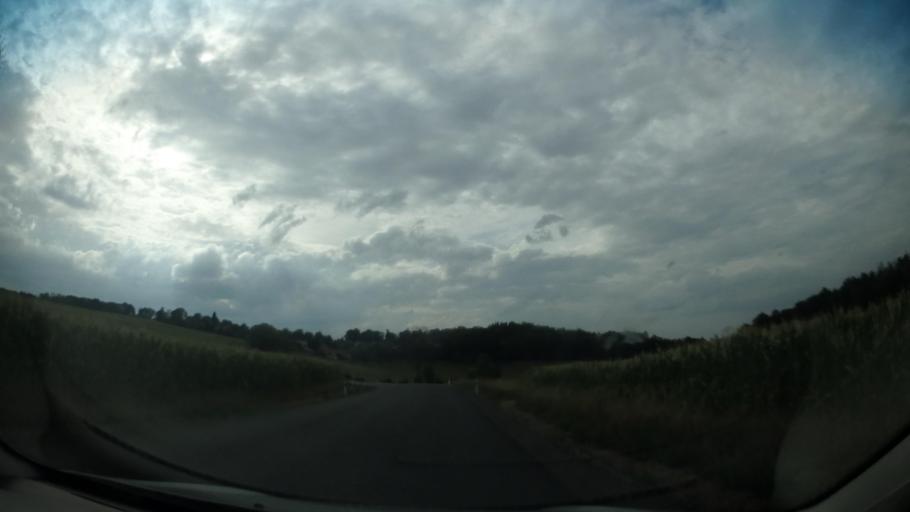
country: CZ
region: Pardubicky
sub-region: Okres Chrudim
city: Sec
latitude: 49.8210
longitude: 15.7017
